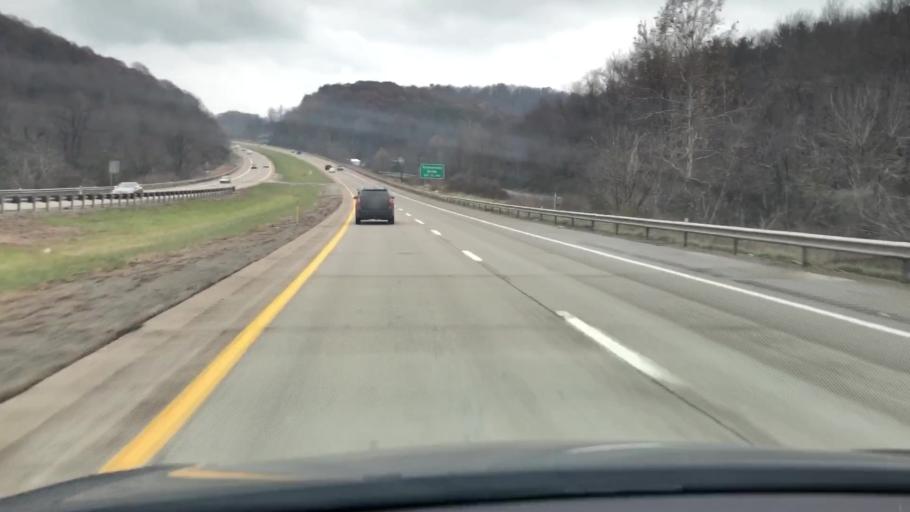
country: US
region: Pennsylvania
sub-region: Westmoreland County
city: New Stanton
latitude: 40.2112
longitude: -79.5898
